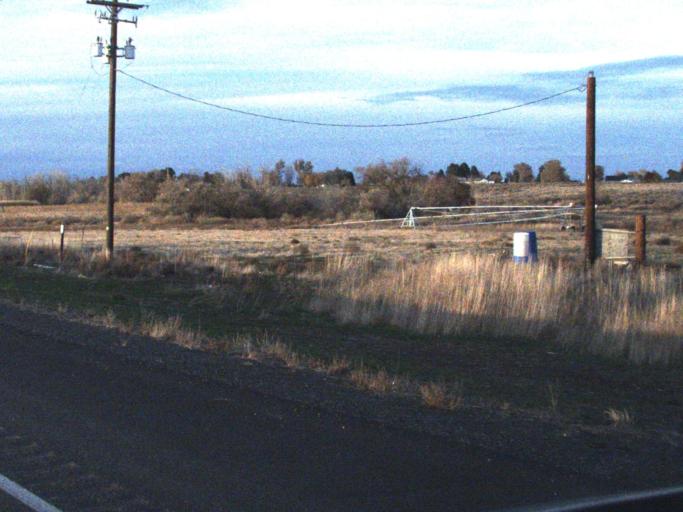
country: US
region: Washington
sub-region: Walla Walla County
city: Burbank
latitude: 46.2025
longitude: -119.0031
